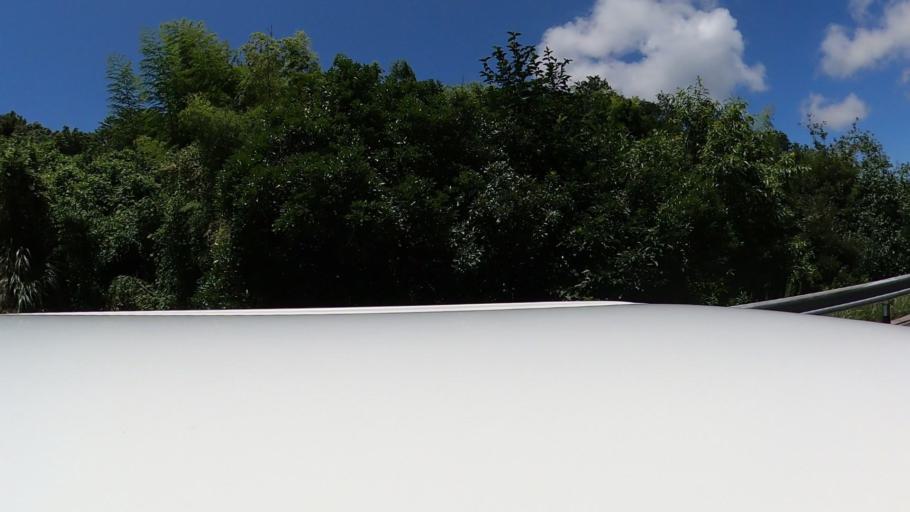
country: JP
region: Miyazaki
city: Nobeoka
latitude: 32.4884
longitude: 131.6464
